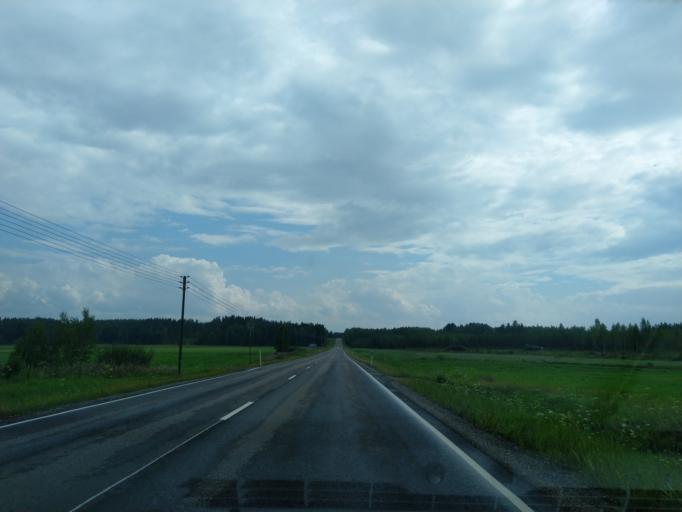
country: FI
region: South Karelia
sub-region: Imatra
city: Parikkala
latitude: 61.6242
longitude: 29.4373
